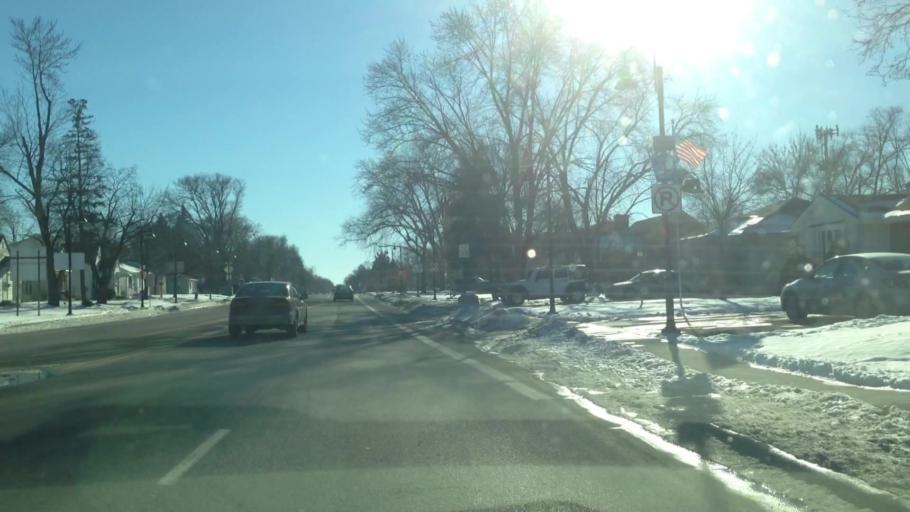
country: US
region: Minnesota
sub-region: Hennepin County
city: Richfield
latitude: 44.8830
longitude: -93.2679
